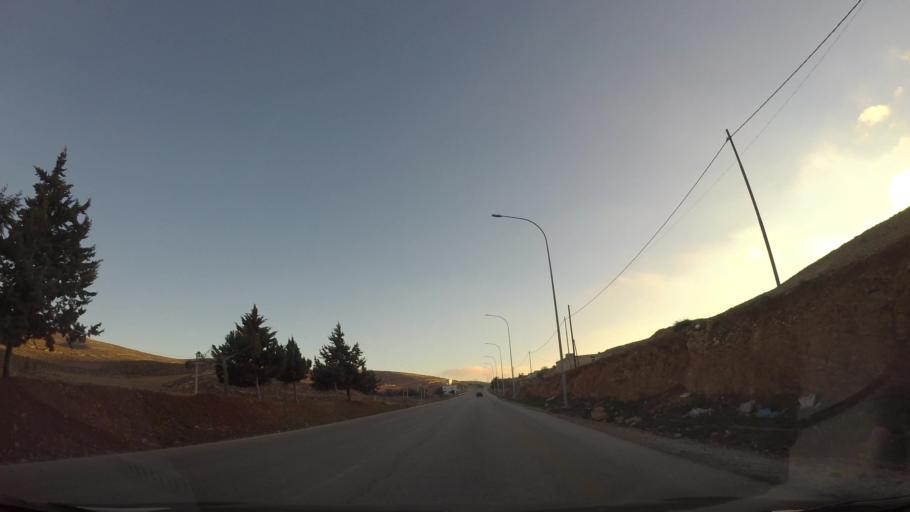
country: JO
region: Ma'an
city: Petra
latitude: 30.4255
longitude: 35.5136
